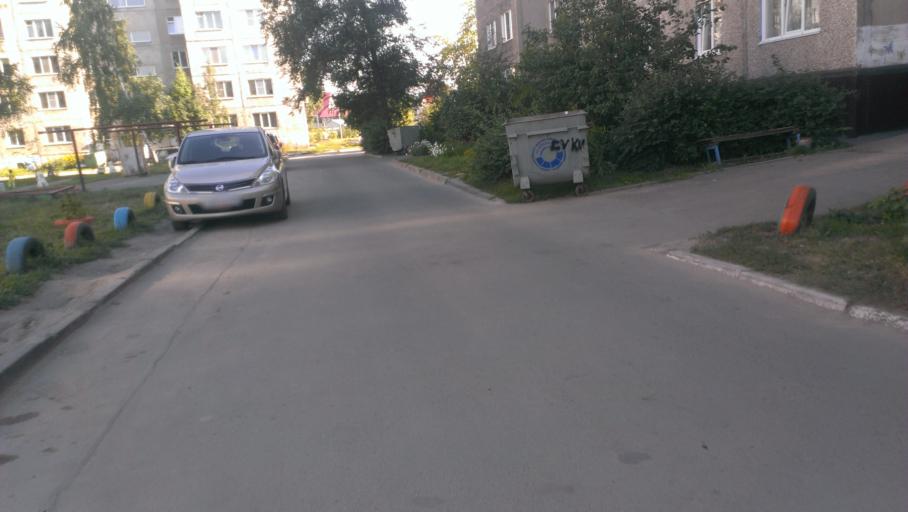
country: RU
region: Altai Krai
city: Novosilikatnyy
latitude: 53.3056
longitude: 83.6236
